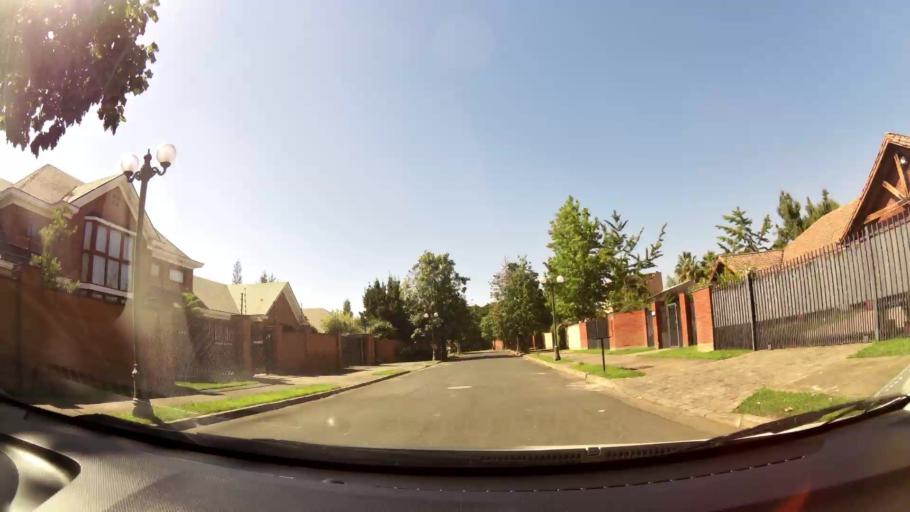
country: CL
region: Maule
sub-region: Provincia de Talca
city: Talca
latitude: -35.4331
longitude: -71.6140
